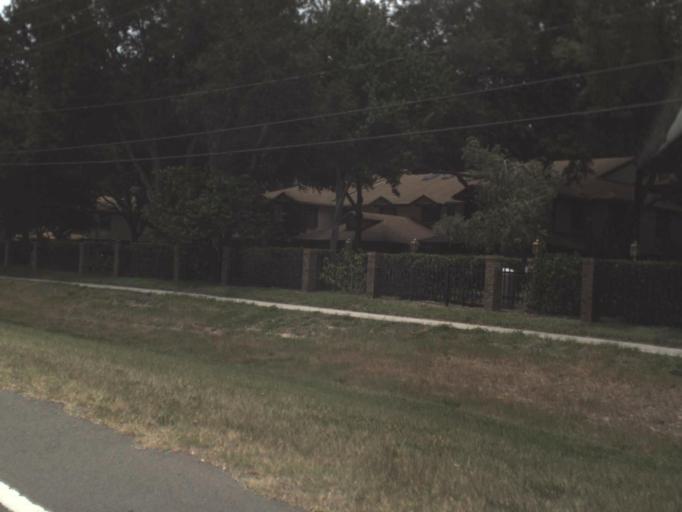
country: US
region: Florida
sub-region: Pinellas County
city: Palm Harbor
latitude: 28.0499
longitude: -82.7685
